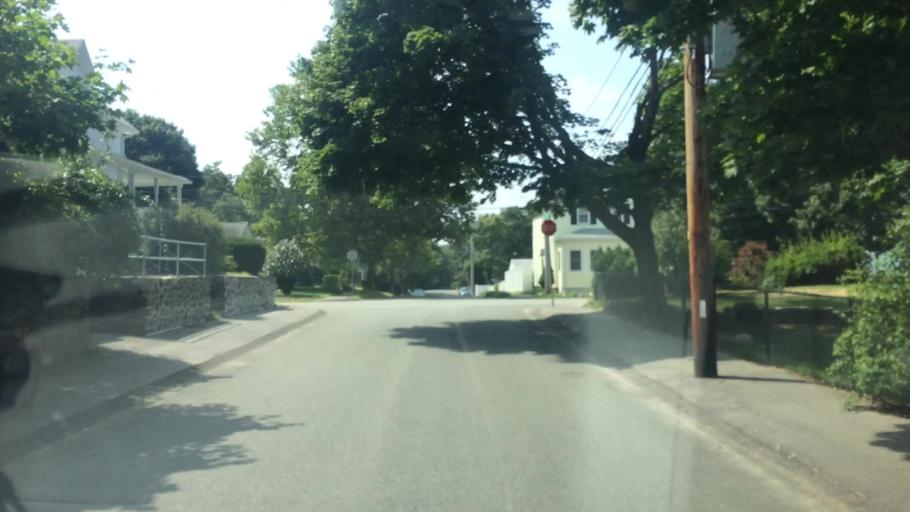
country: US
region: Massachusetts
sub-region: Norfolk County
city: Dedham
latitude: 42.2496
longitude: -71.1470
